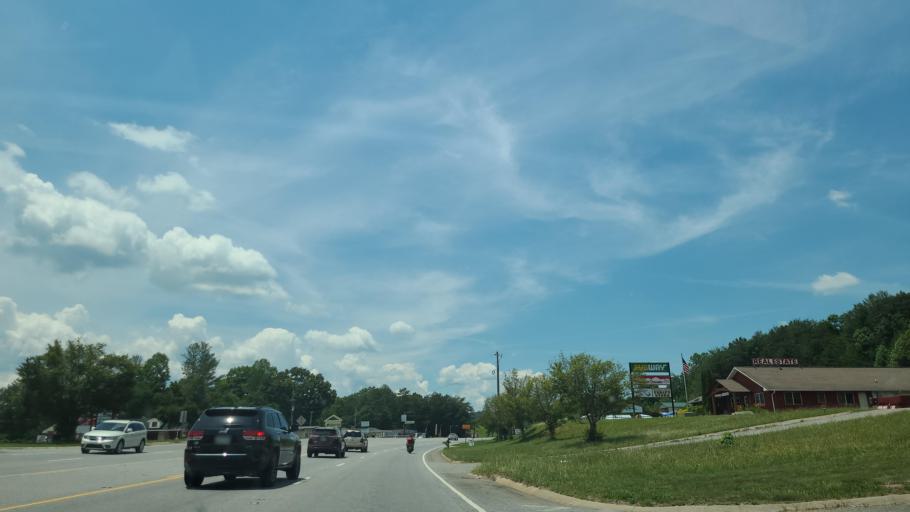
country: US
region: North Carolina
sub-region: Clay County
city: Hayesville
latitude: 35.0347
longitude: -83.8231
